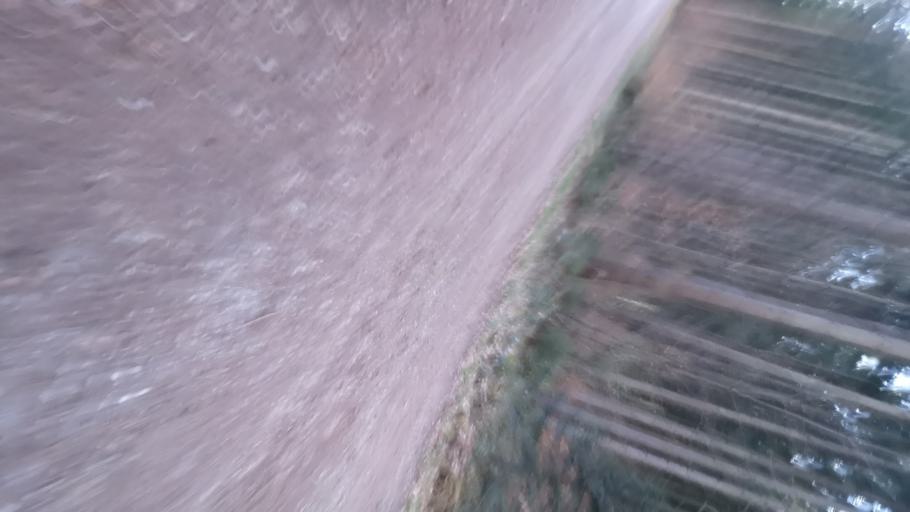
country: DE
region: Bavaria
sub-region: Upper Bavaria
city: Planegg
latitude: 48.0680
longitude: 11.4283
